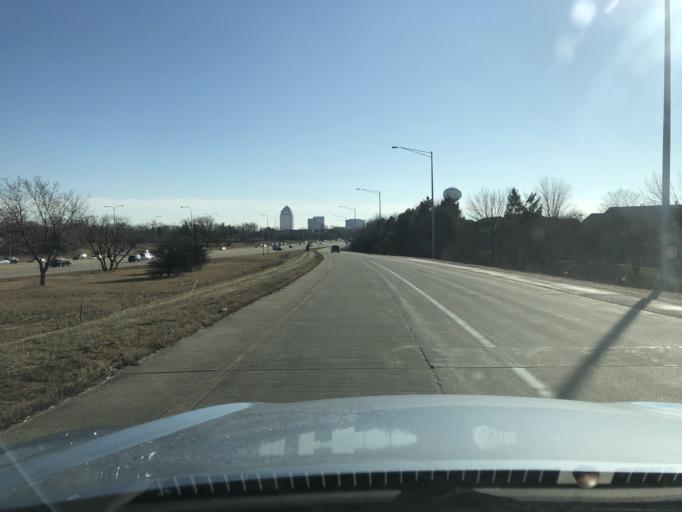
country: US
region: Illinois
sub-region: DuPage County
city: Itasca
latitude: 42.0029
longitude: -88.0278
